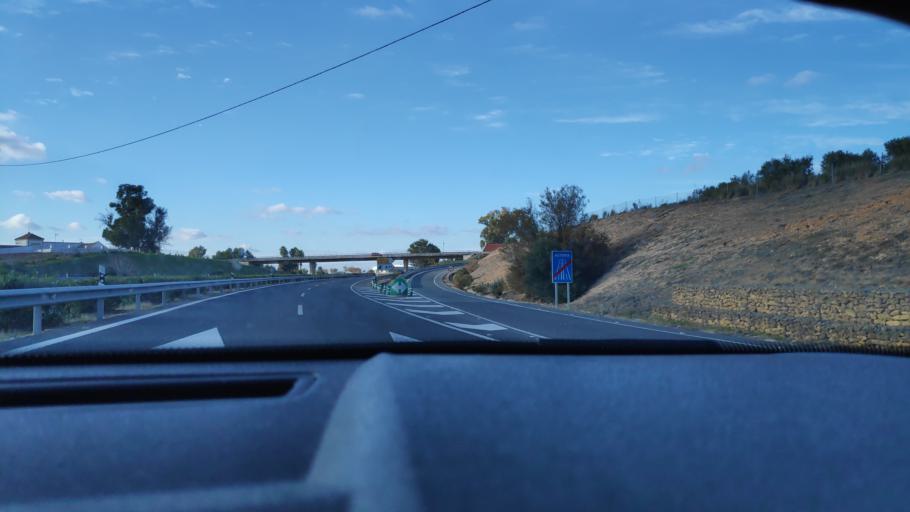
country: ES
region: Andalusia
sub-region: Provincia de Sevilla
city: La Luisiana
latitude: 37.5231
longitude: -5.2573
